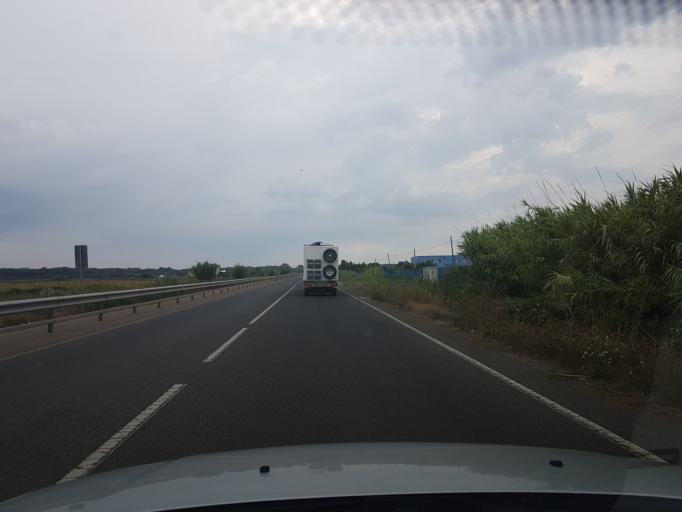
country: IT
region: Sardinia
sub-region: Provincia di Oristano
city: Cabras
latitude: 39.9131
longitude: 8.5378
